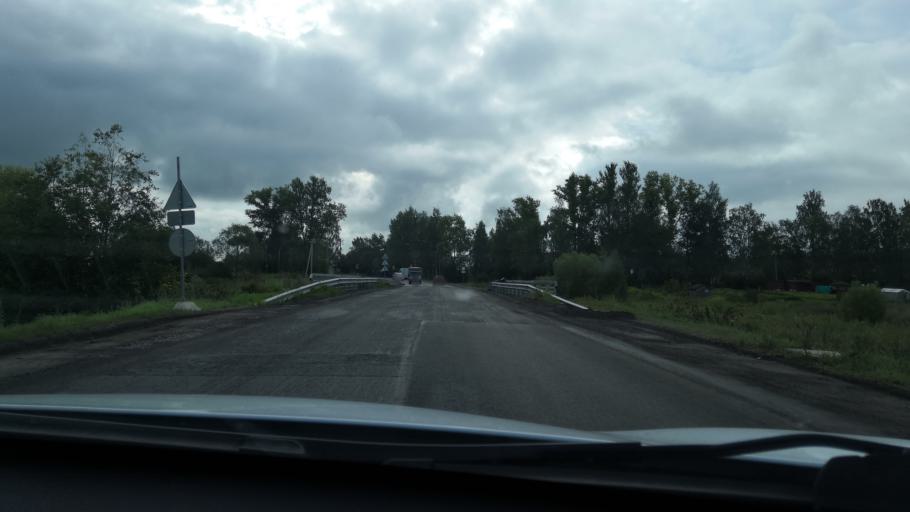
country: RU
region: St.-Petersburg
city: Tyarlevo
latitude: 59.7114
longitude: 30.4678
